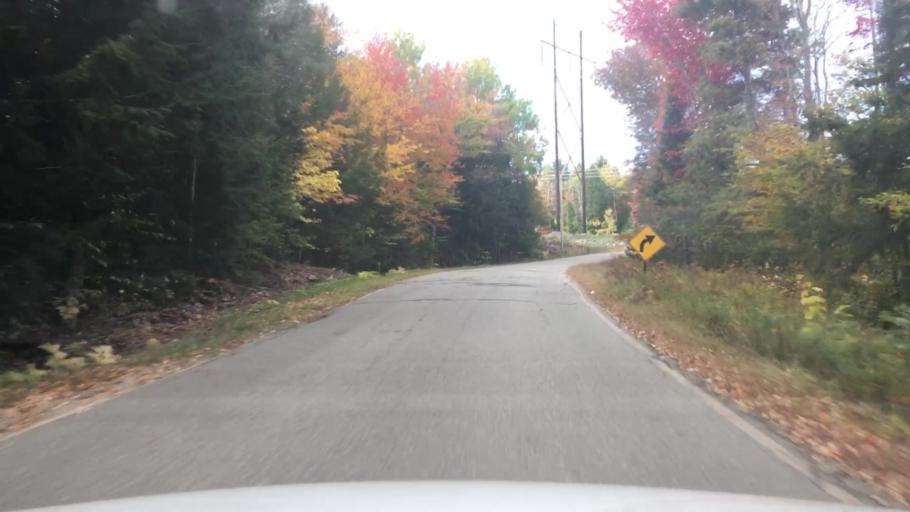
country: US
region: Maine
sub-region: Knox County
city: Washington
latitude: 44.3250
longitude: -69.3652
